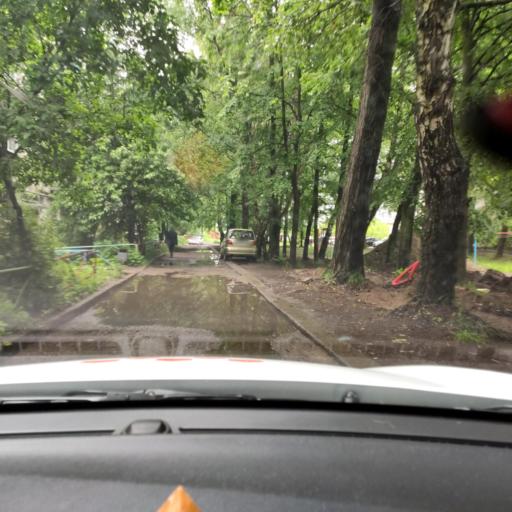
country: RU
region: Tatarstan
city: Staroye Arakchino
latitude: 55.8784
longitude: 49.0179
